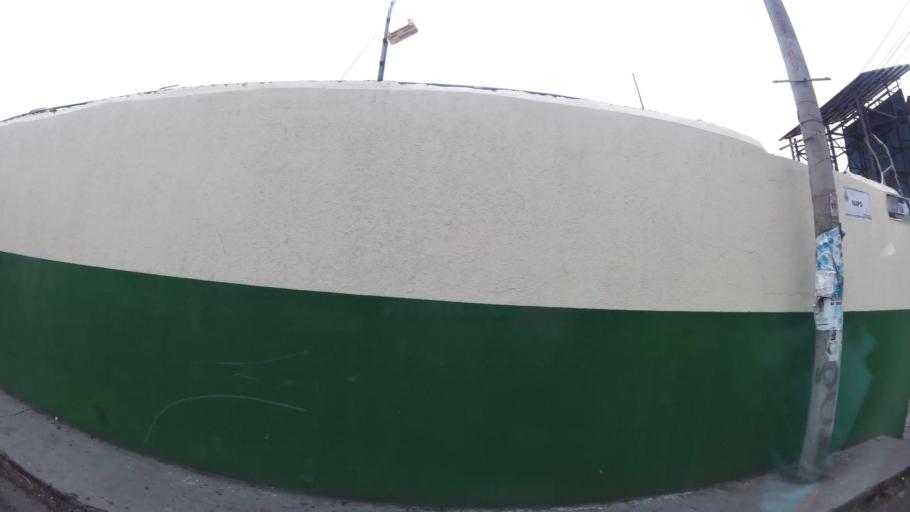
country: EC
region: Cotopaxi
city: Latacunga
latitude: -0.9322
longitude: -78.6130
